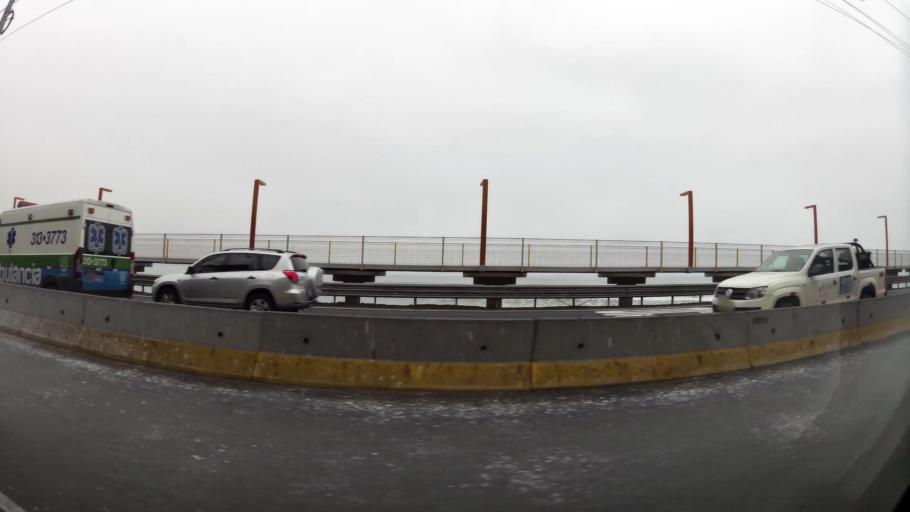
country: PE
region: Lima
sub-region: Lima
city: San Isidro
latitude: -12.1230
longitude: -77.0429
